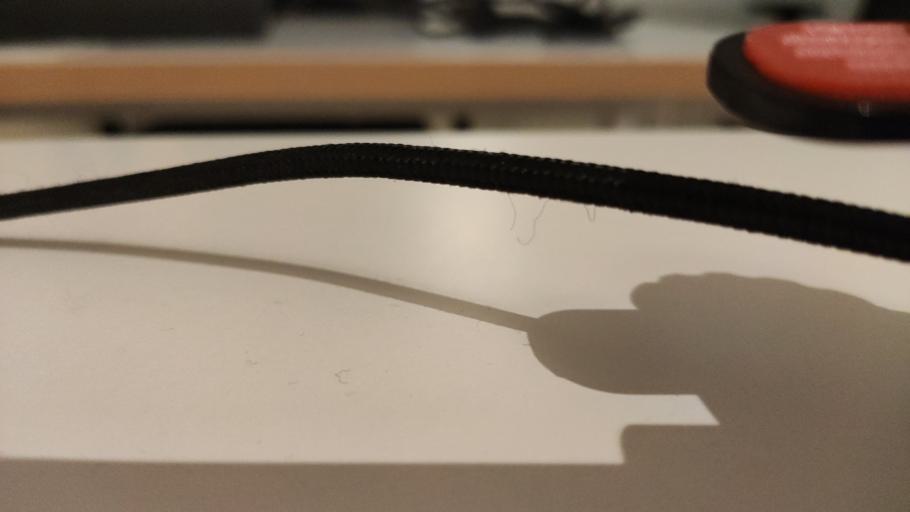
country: RU
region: Moskovskaya
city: Zhilevo
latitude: 55.0996
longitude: 38.0662
